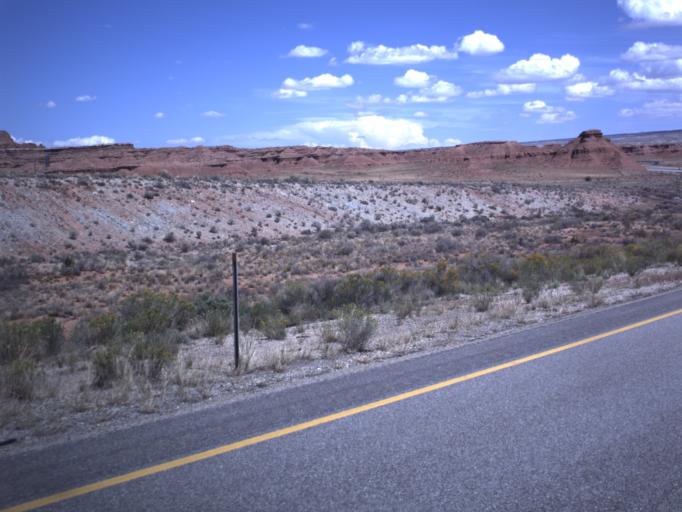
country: US
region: Utah
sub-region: Emery County
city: Ferron
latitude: 38.8385
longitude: -111.0802
